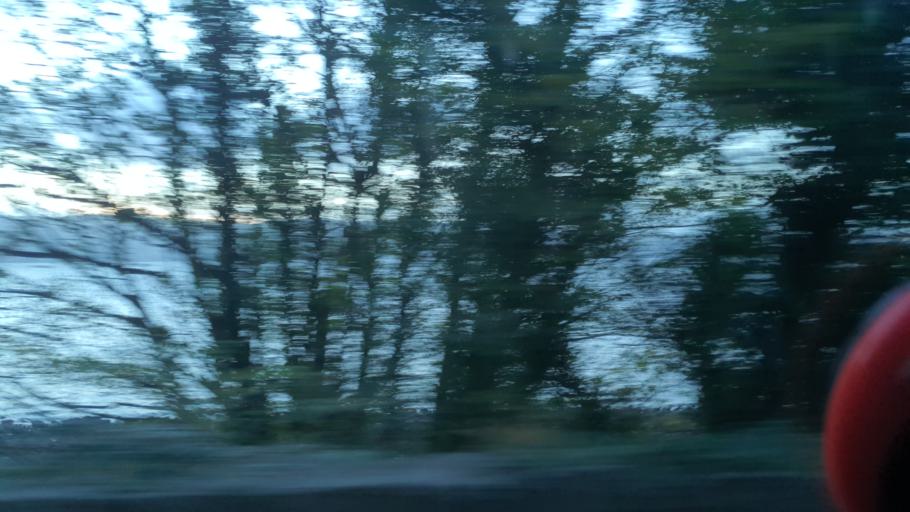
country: GB
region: Northern Ireland
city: Rostrevor
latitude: 54.0900
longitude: -6.1898
